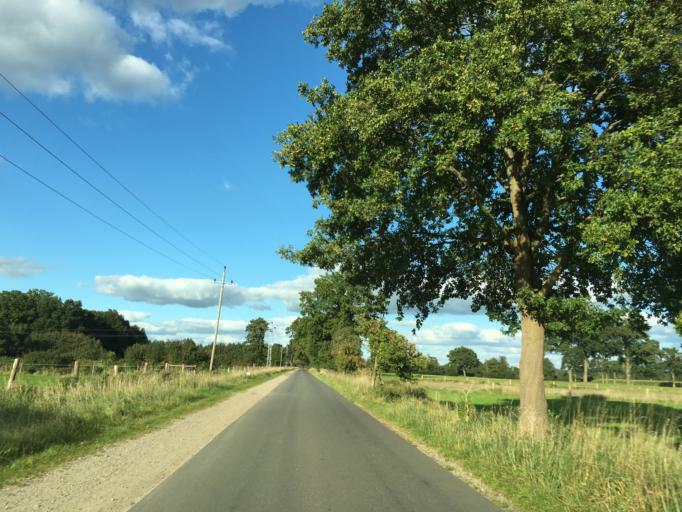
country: DE
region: Lower Saxony
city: Salzhausen
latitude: 53.2398
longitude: 10.1804
